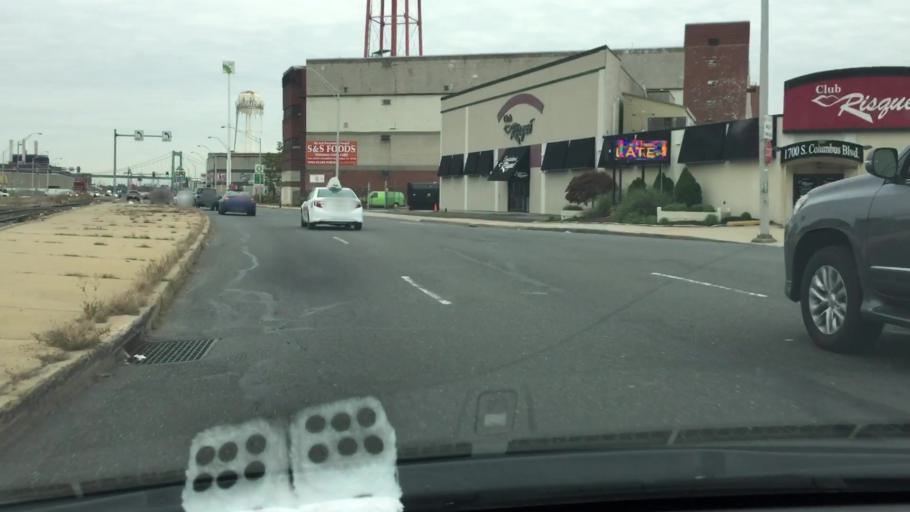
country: US
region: New Jersey
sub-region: Camden County
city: Camden
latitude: 39.9260
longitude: -75.1448
